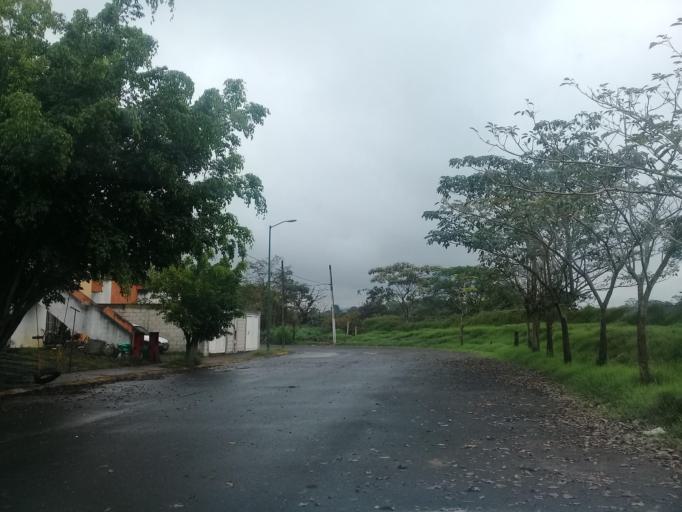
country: MX
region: Veracruz
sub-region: Amatlan de los Reyes
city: Trapiche Viejo
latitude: 18.8376
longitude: -96.9501
